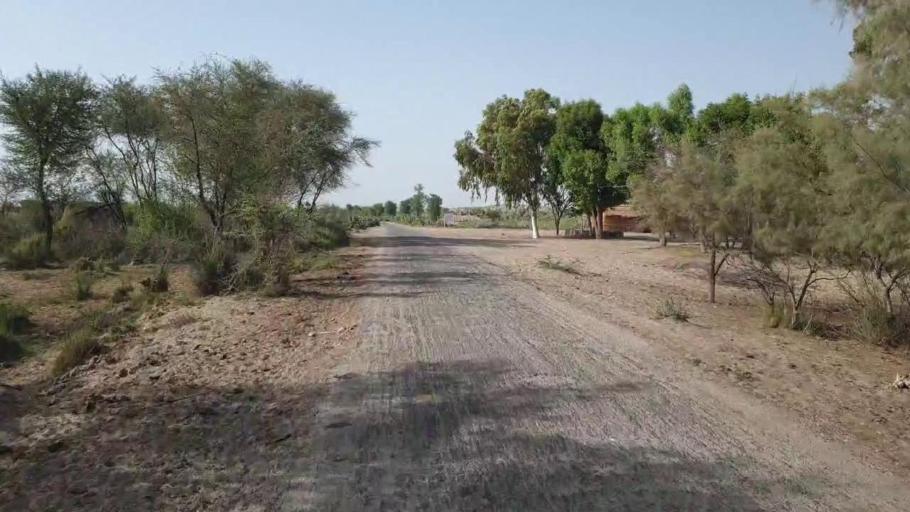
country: PK
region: Sindh
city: Kandiari
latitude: 26.7073
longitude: 68.9641
